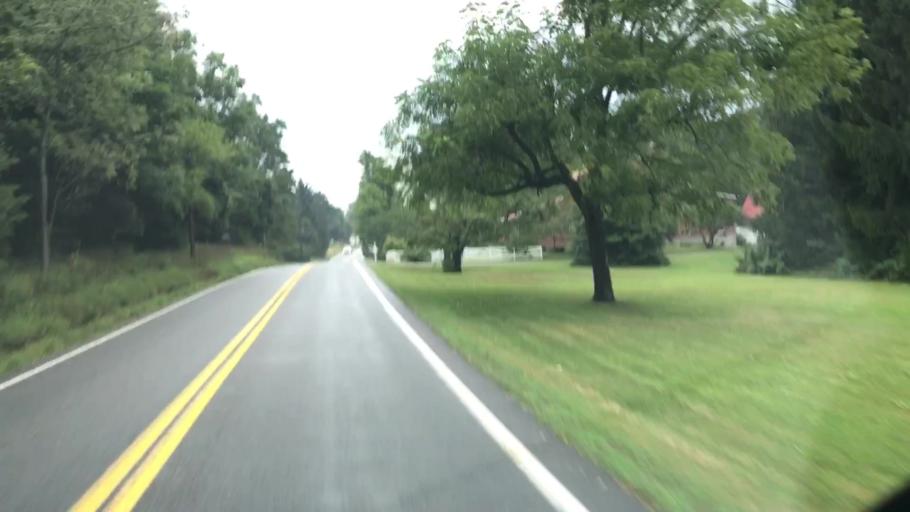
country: US
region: Pennsylvania
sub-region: Perry County
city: New Bloomfield
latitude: 40.3945
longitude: -77.1278
